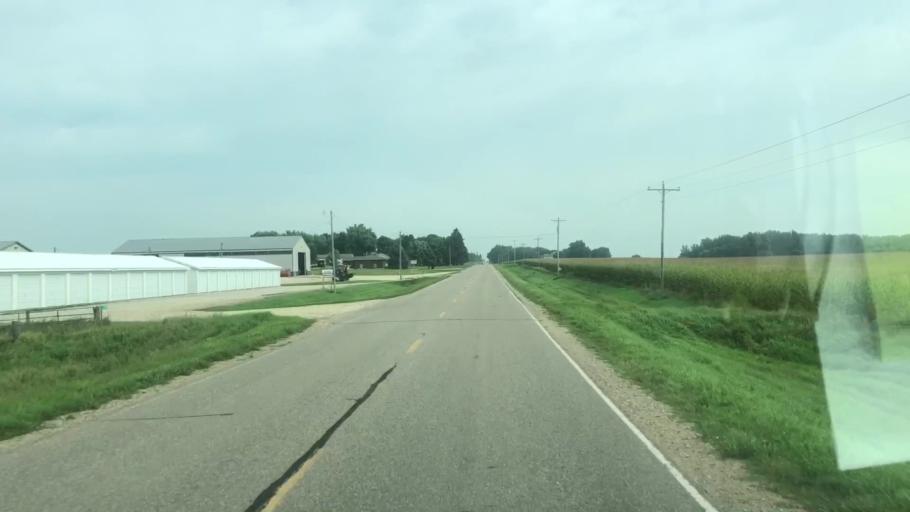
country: US
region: Iowa
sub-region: O'Brien County
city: Sheldon
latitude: 43.1927
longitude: -95.8622
